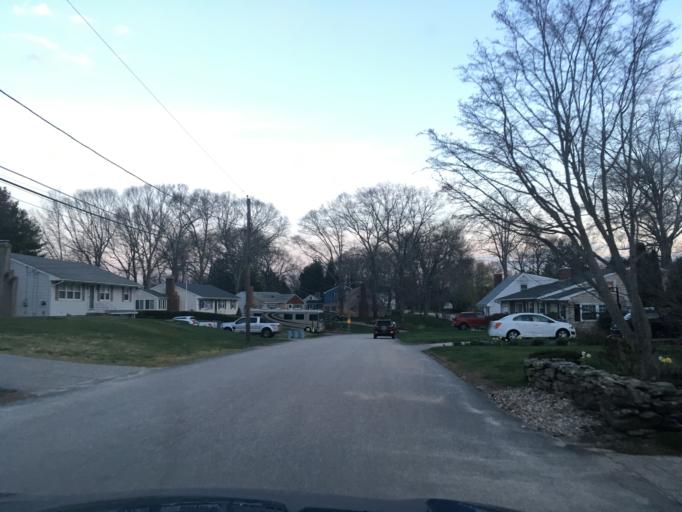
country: US
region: Rhode Island
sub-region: Kent County
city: East Greenwich
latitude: 41.6231
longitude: -71.4880
